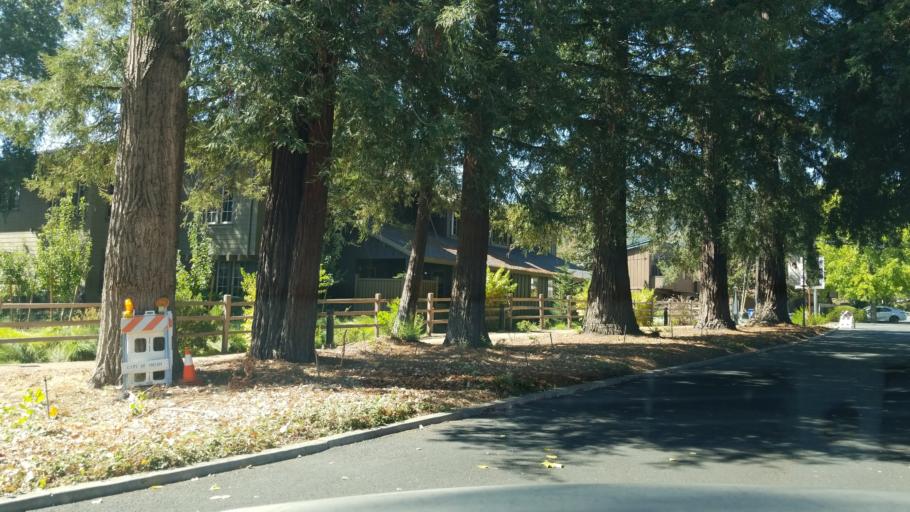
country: US
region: California
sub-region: Mendocino County
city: Ukiah
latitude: 39.1474
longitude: -123.2052
